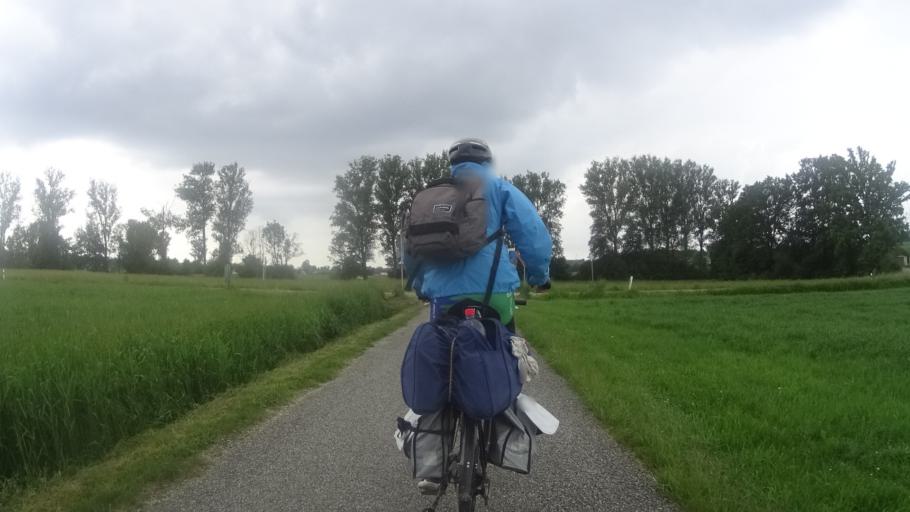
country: DE
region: Bavaria
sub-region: Lower Bavaria
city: Hebertsfelden
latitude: 48.4182
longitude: 12.8446
